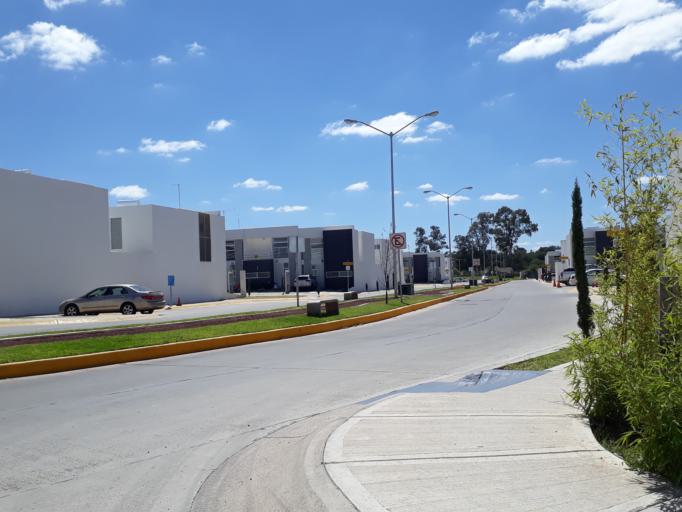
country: MX
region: Aguascalientes
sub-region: Aguascalientes
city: San Sebastian [Fraccionamiento]
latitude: 21.8309
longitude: -102.3012
